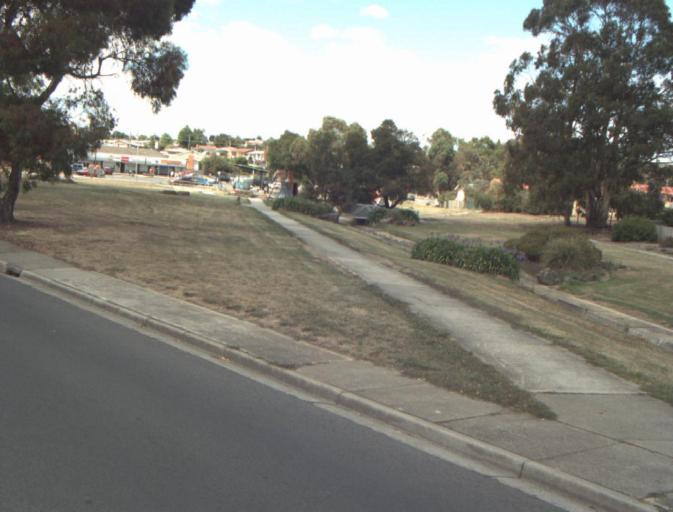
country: AU
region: Tasmania
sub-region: Launceston
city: Newstead
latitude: -41.4169
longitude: 147.1744
